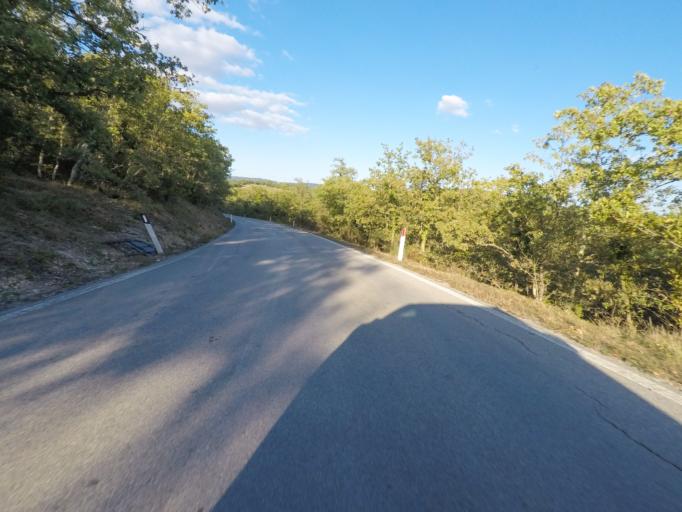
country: IT
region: Tuscany
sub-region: Provincia di Siena
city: Radda in Chianti
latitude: 43.4574
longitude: 11.3861
